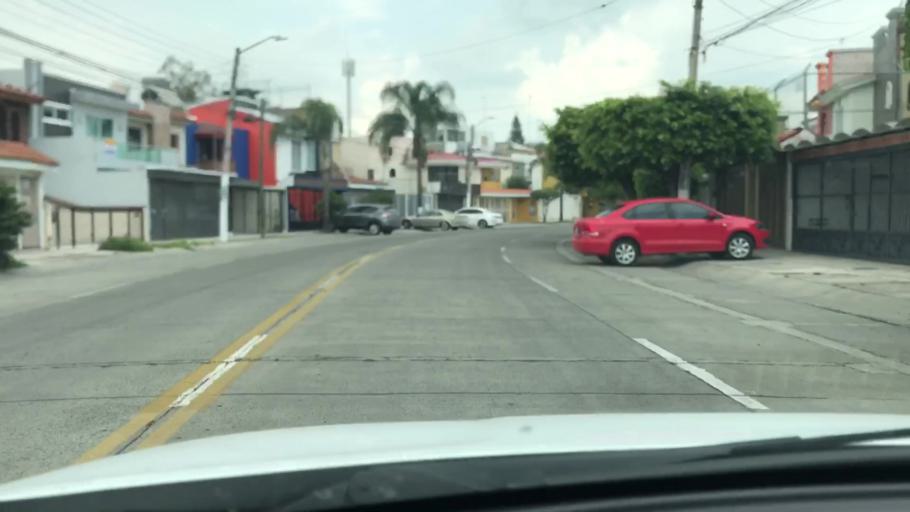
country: MX
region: Jalisco
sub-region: Tlajomulco de Zuniga
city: Palomar
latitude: 20.6341
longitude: -103.4353
